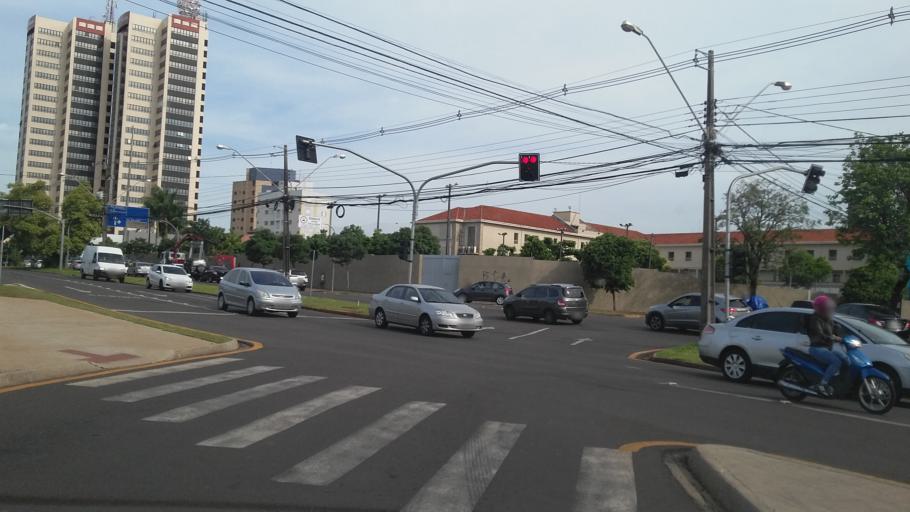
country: BR
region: Parana
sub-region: Londrina
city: Londrina
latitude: -23.3009
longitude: -51.1808
